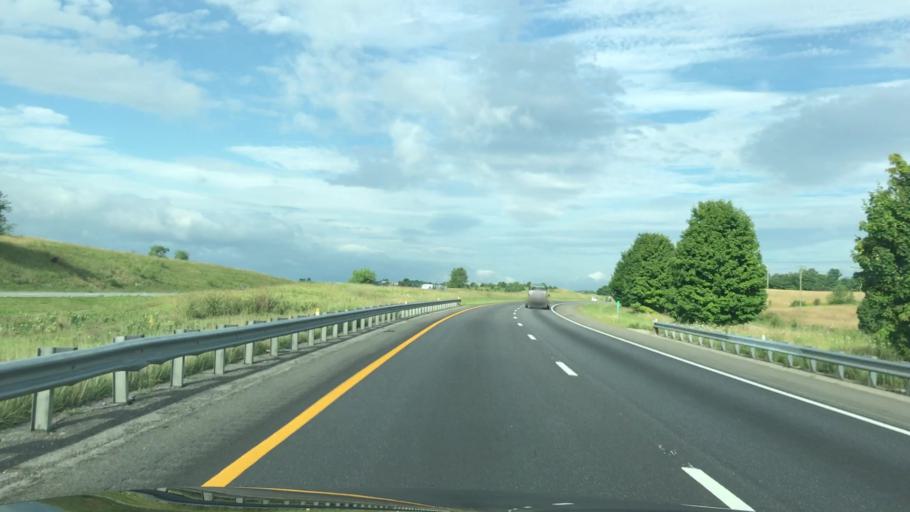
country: US
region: Virginia
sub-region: Montgomery County
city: Christiansburg
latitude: 37.0953
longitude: -80.4799
